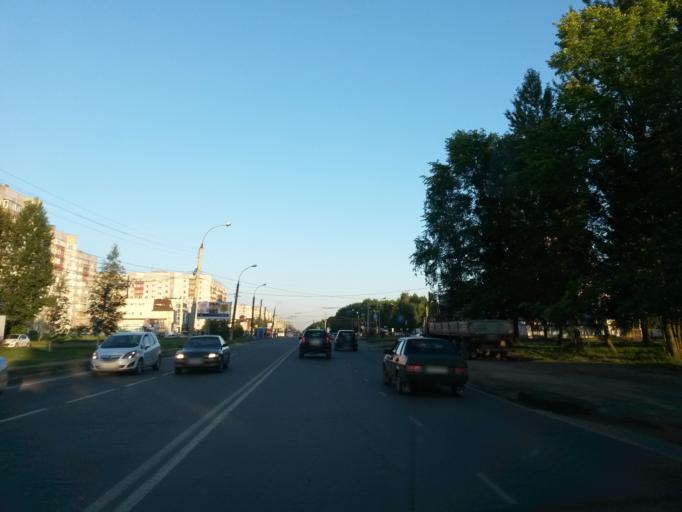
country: RU
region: Jaroslavl
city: Yaroslavl
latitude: 57.6971
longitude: 39.7654
